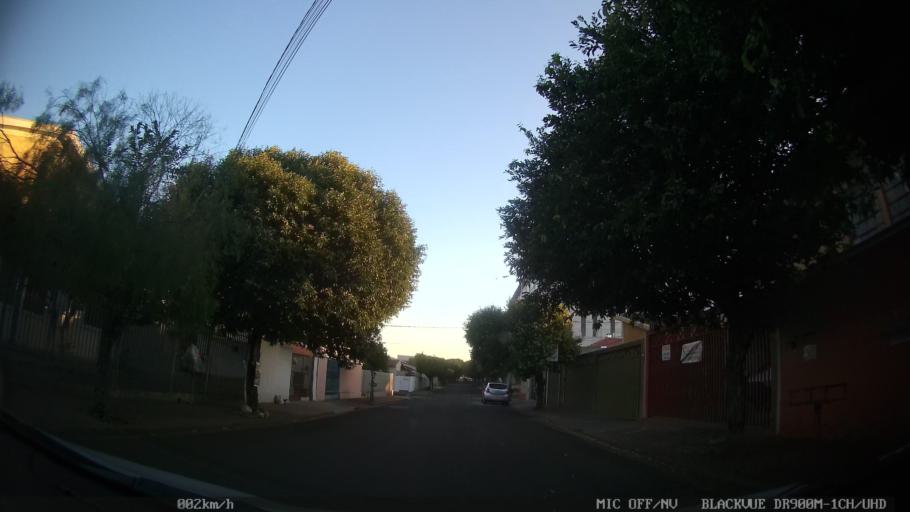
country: BR
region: Sao Paulo
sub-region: Sao Jose Do Rio Preto
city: Sao Jose do Rio Preto
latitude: -20.8010
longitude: -49.3658
